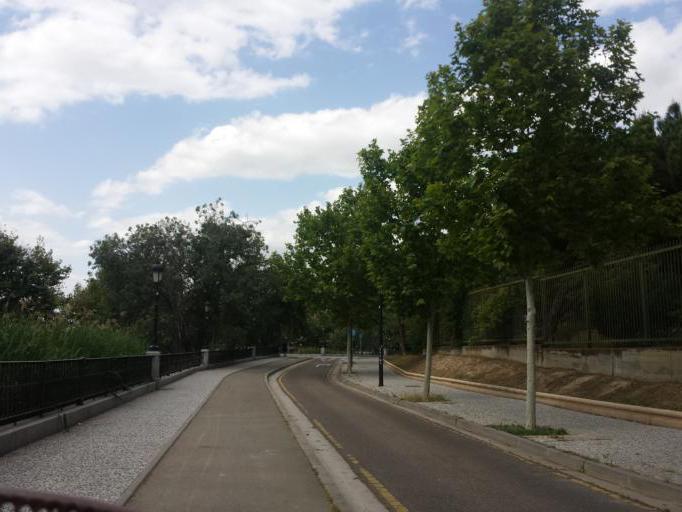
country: ES
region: Aragon
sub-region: Provincia de Zaragoza
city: Delicias
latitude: 41.6325
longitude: -0.8914
